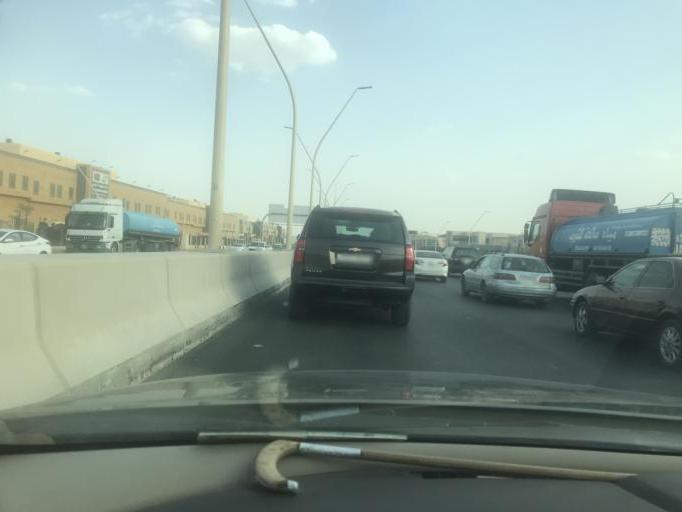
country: SA
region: Ar Riyad
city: Riyadh
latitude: 24.8148
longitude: 46.6677
